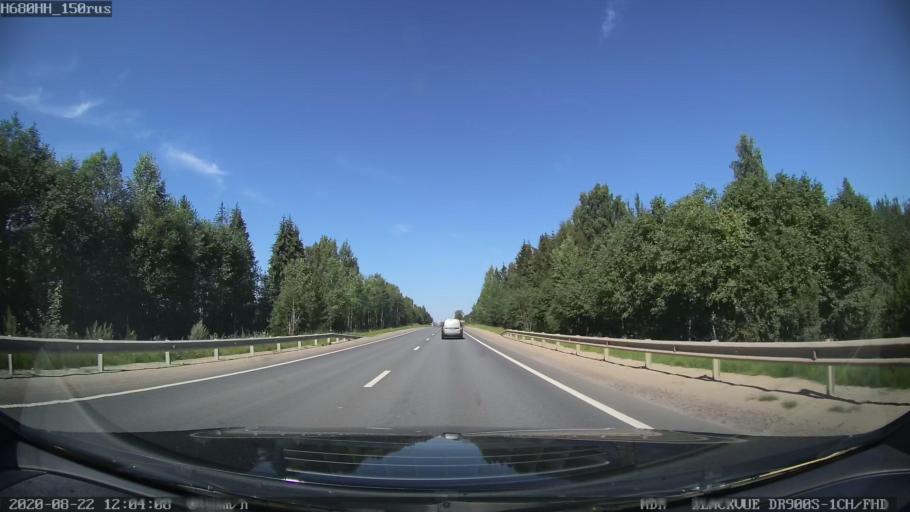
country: RU
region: Tverskaya
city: Rameshki
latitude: 57.2643
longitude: 36.0766
